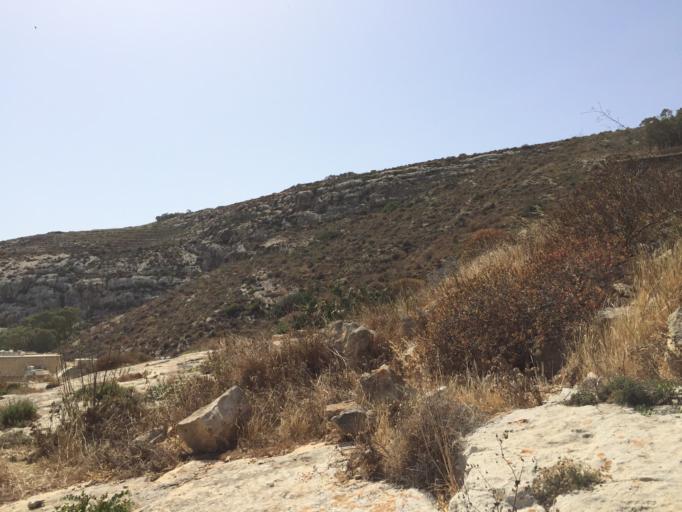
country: MT
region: Saint Lucia
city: Saint Lucia
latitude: 36.0324
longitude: 14.2199
